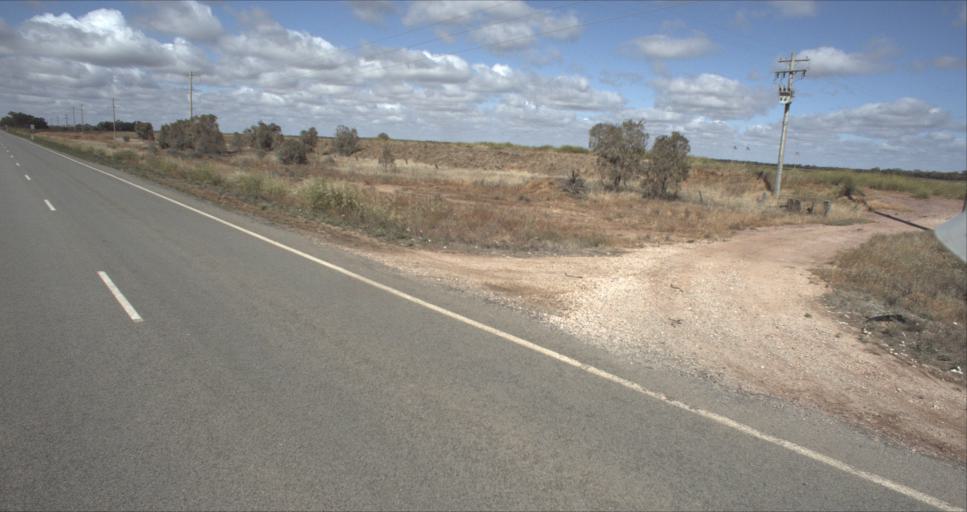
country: AU
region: New South Wales
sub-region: Murrumbidgee Shire
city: Darlington Point
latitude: -34.5487
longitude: 146.1709
